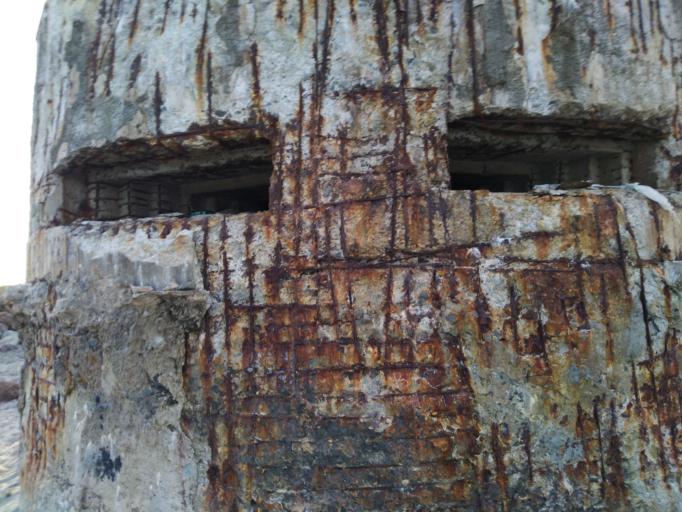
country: BG
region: Burgas
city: Aheloy
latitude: 42.6239
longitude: 27.6347
